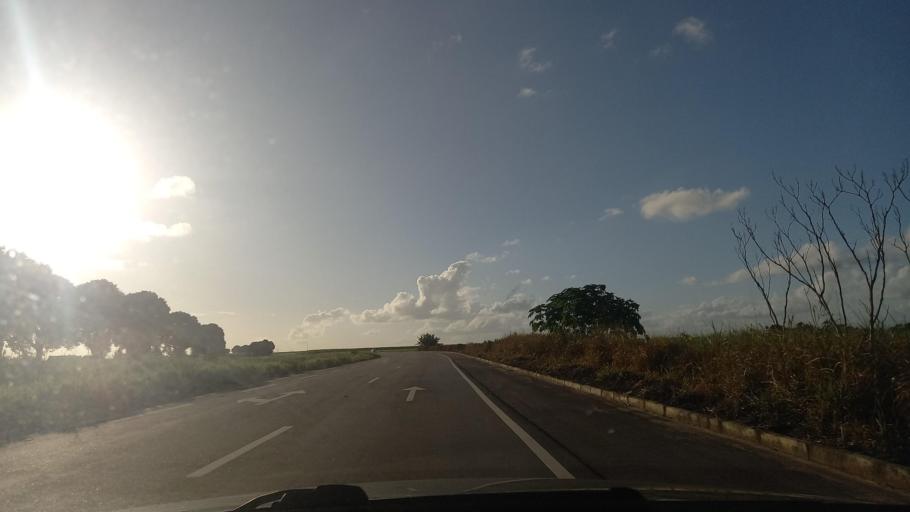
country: BR
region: Alagoas
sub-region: Campo Alegre
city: Campo Alegre
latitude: -9.8086
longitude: -36.2596
